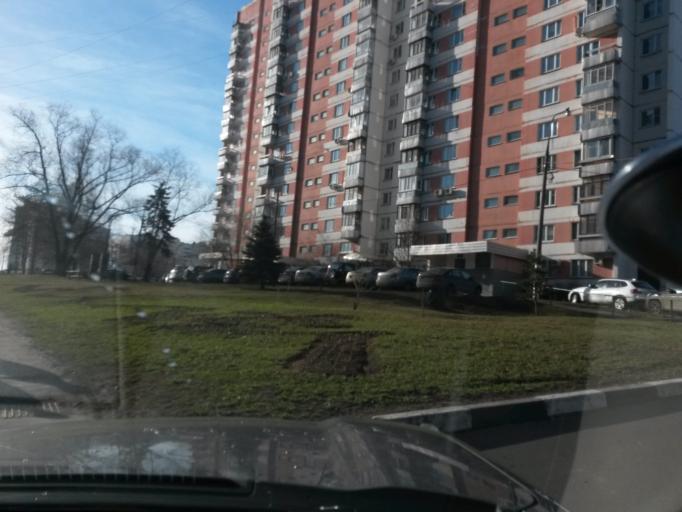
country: RU
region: Moscow
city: Annino
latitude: 55.5636
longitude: 37.5819
